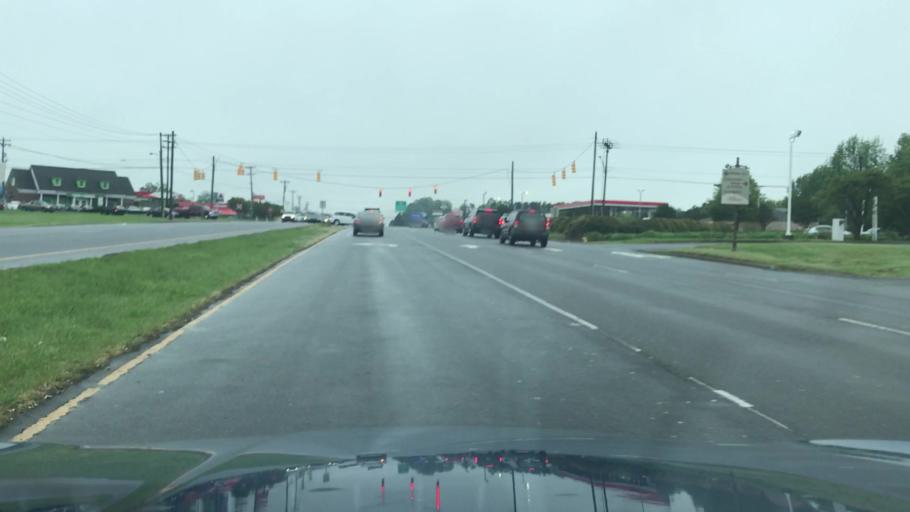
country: US
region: North Carolina
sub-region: Mecklenburg County
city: Matthews
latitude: 35.1197
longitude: -80.6988
